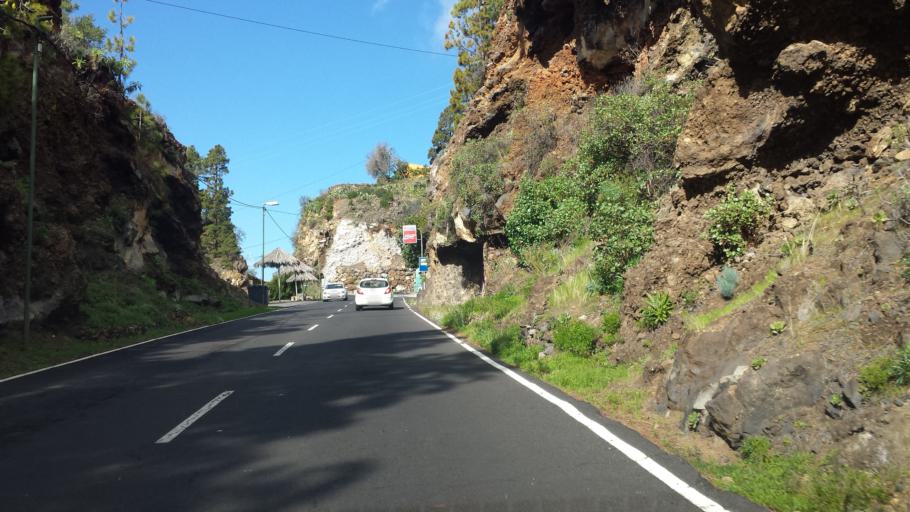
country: ES
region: Canary Islands
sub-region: Provincia de Santa Cruz de Tenerife
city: Tijarafe
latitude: 28.7260
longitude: -17.9604
